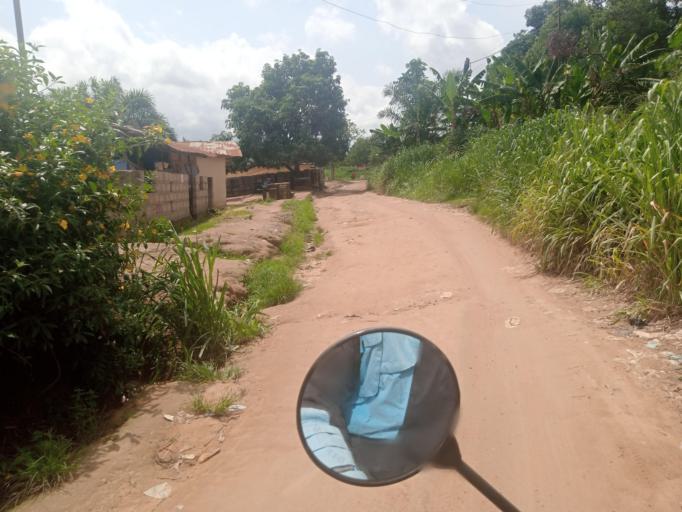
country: SL
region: Southern Province
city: Bo
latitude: 7.9623
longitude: -11.7515
